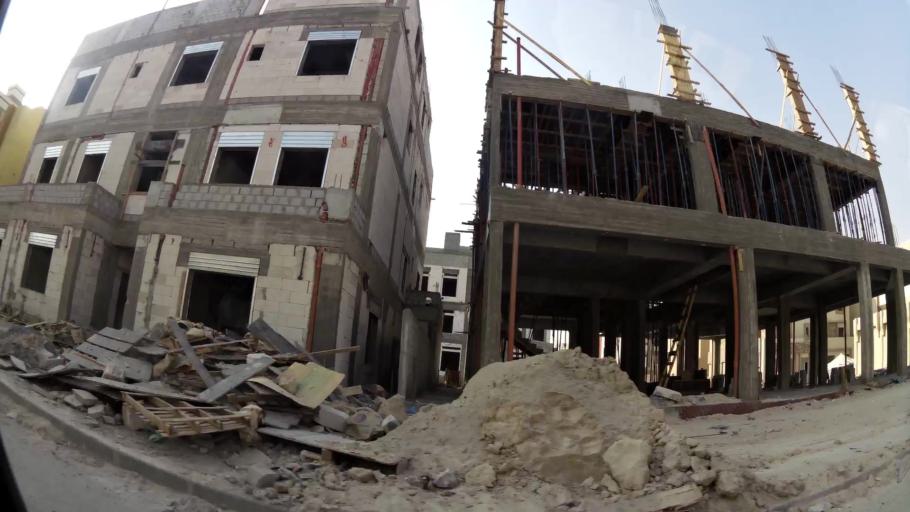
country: KW
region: Al Asimah
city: Ar Rabiyah
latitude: 29.3262
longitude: 47.8068
